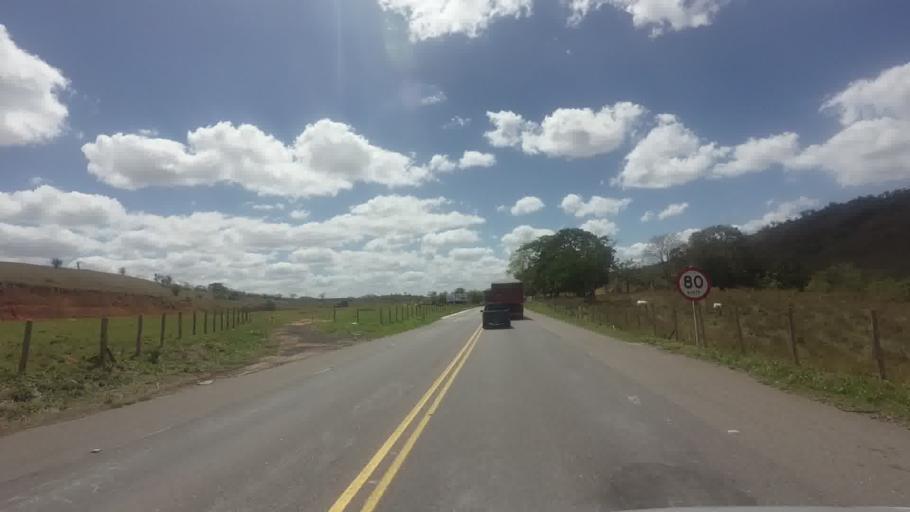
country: BR
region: Minas Gerais
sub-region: Recreio
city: Recreio
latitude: -21.6664
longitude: -42.3856
